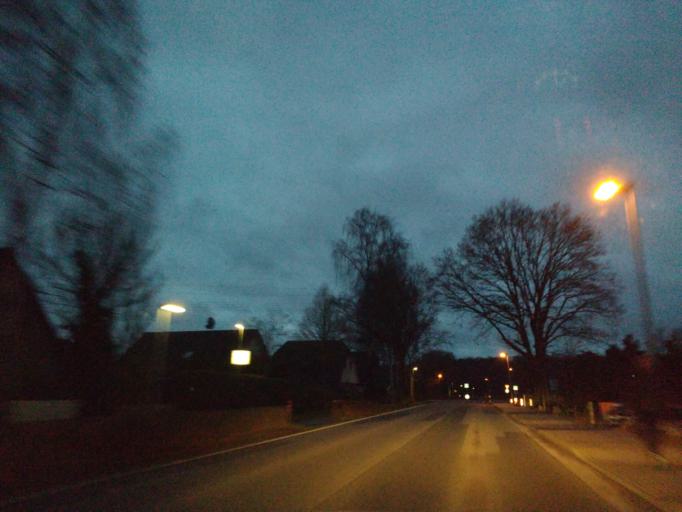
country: DE
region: Schleswig-Holstein
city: Ratekau
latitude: 53.9427
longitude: 10.7278
